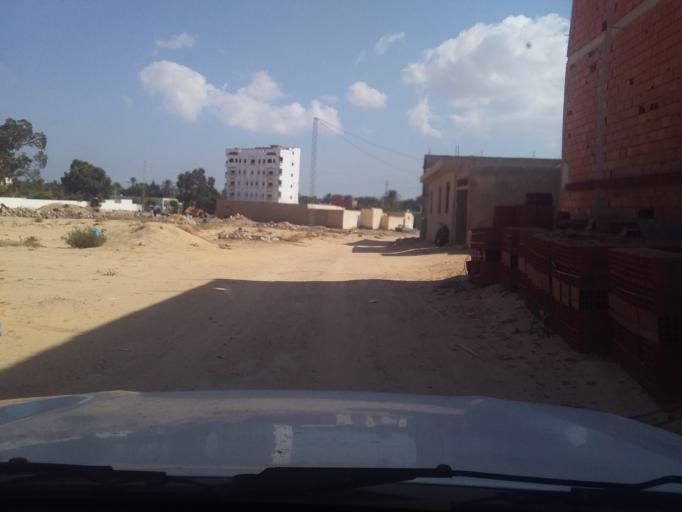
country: TN
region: Qabis
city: Gabes
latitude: 33.6258
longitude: 10.2804
